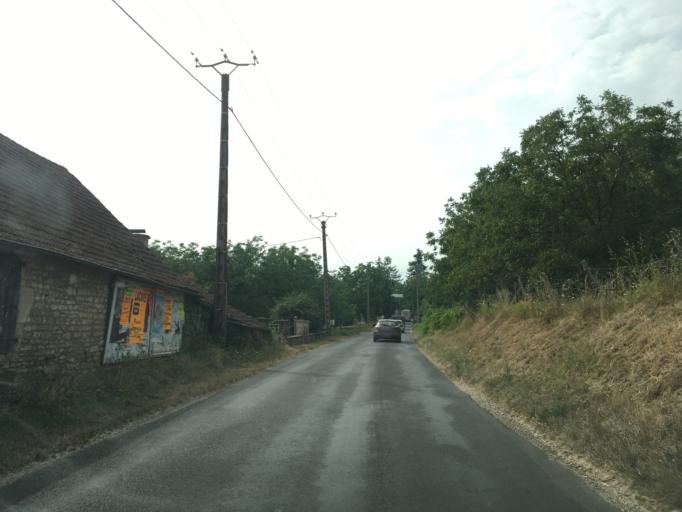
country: FR
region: Midi-Pyrenees
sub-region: Departement du Lot
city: Souillac
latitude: 44.8533
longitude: 1.5177
